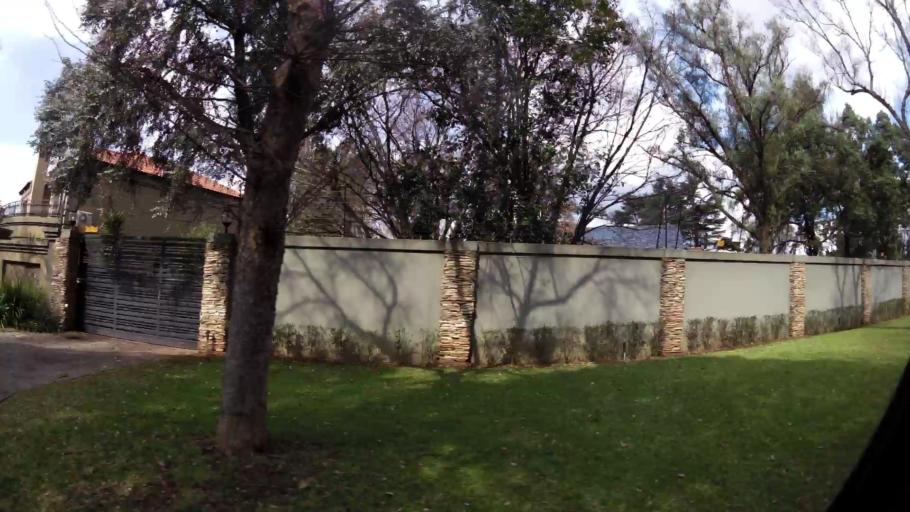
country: ZA
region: Gauteng
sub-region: Sedibeng District Municipality
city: Vanderbijlpark
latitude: -26.7411
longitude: 27.8350
